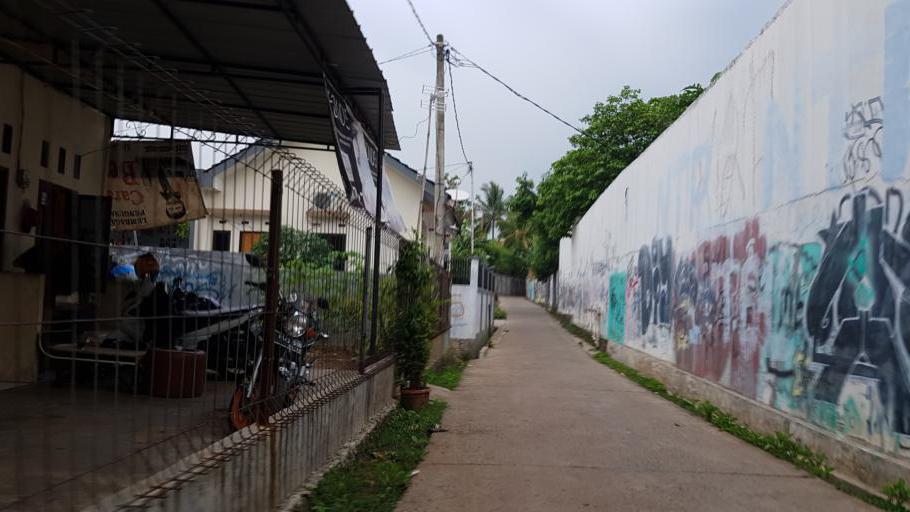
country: ID
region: West Java
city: Pamulang
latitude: -6.3414
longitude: 106.7902
